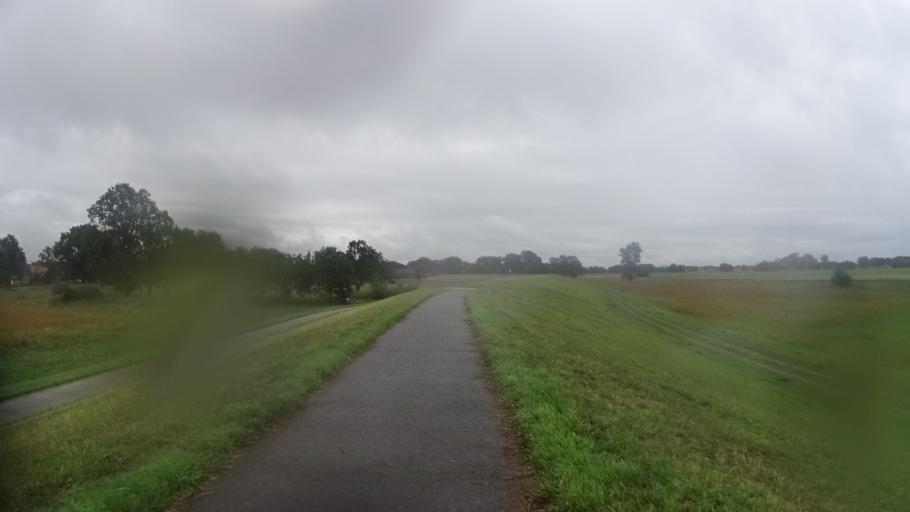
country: DE
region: Lower Saxony
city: Damnatz
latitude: 53.1746
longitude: 11.1594
